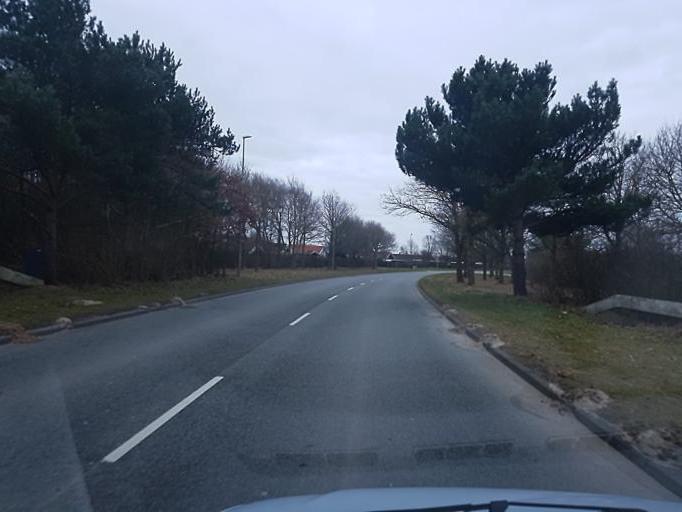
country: DK
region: South Denmark
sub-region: Esbjerg Kommune
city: Esbjerg
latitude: 55.5245
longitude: 8.4297
